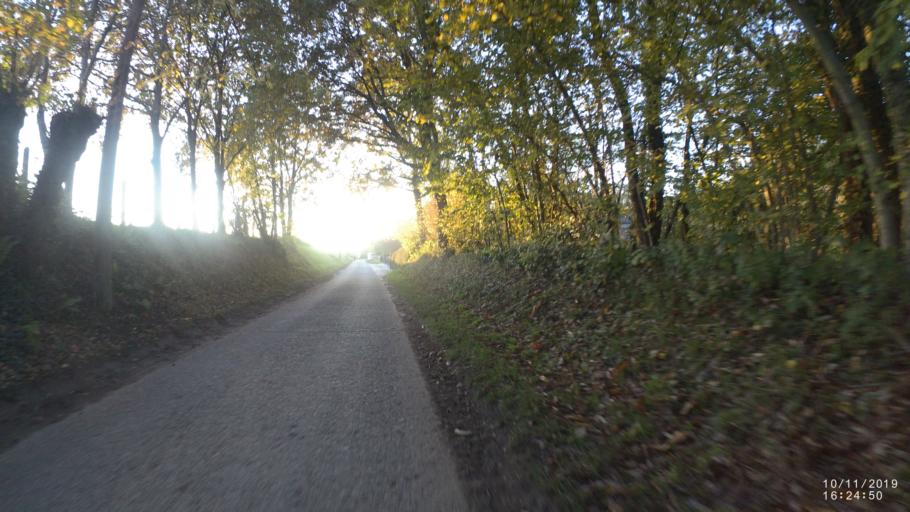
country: BE
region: Flanders
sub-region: Provincie Vlaams-Brabant
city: Lubbeek
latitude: 50.8767
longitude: 4.8291
